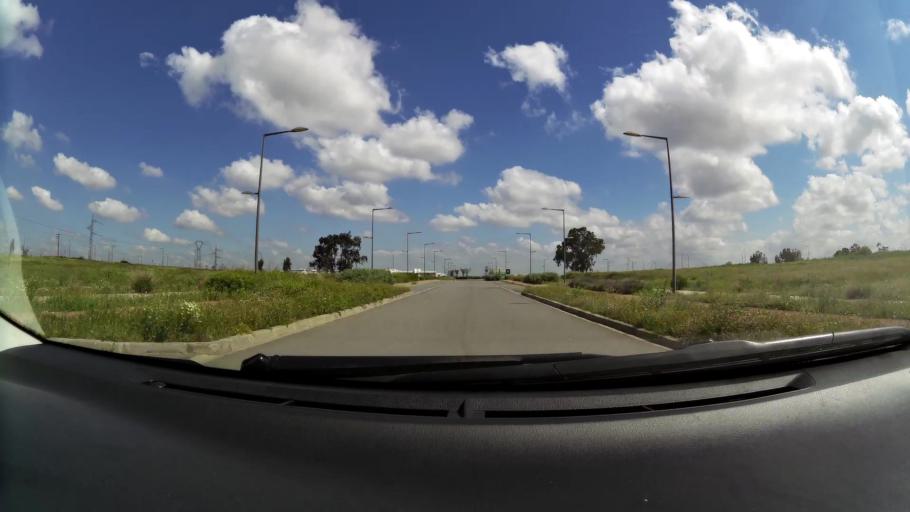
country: MA
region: Grand Casablanca
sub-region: Nouaceur
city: Bouskoura
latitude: 33.4974
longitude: -7.6072
